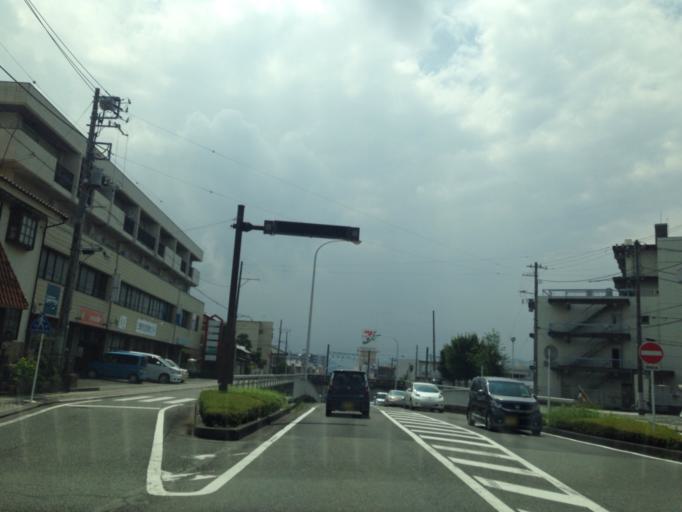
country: JP
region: Shizuoka
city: Mishima
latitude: 35.1171
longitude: 138.9195
